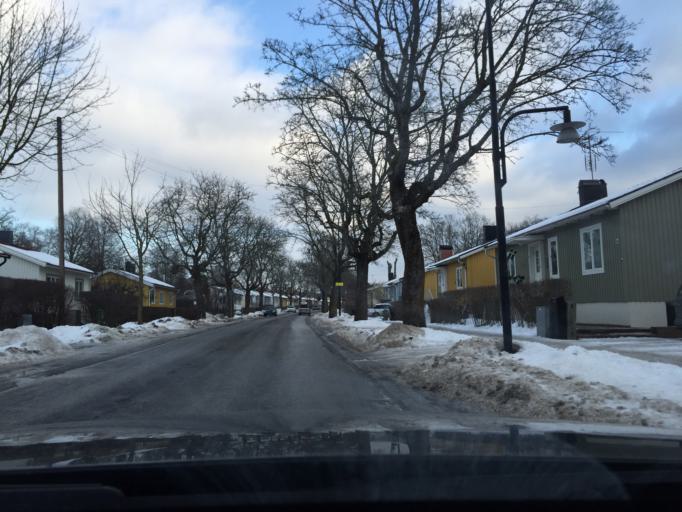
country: SE
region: Stockholm
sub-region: Stockholms Kommun
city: Bromma
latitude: 59.3453
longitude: 17.9175
